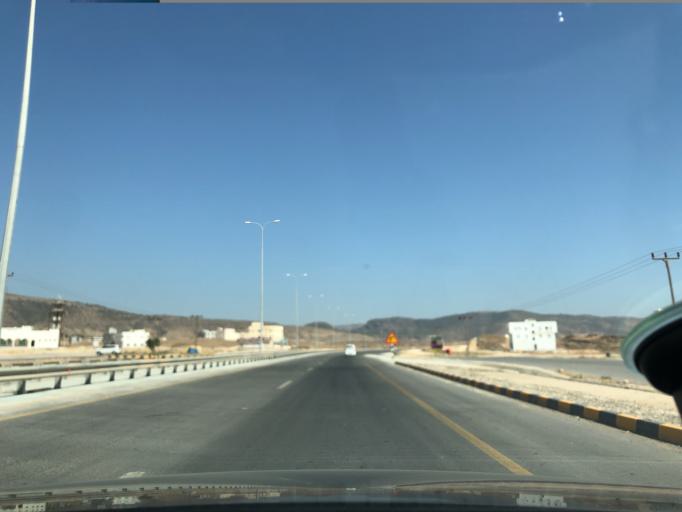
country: OM
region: Zufar
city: Salalah
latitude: 17.0521
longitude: 54.4016
